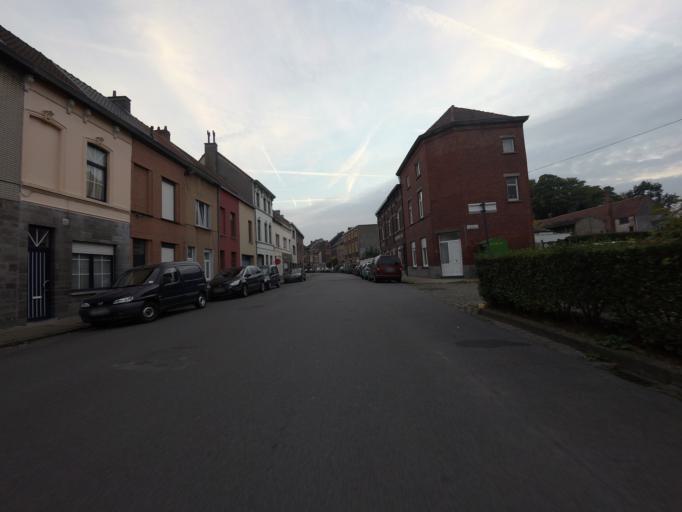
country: BE
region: Flanders
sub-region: Provincie Oost-Vlaanderen
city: Ledeberg
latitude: 51.0632
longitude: 3.7469
